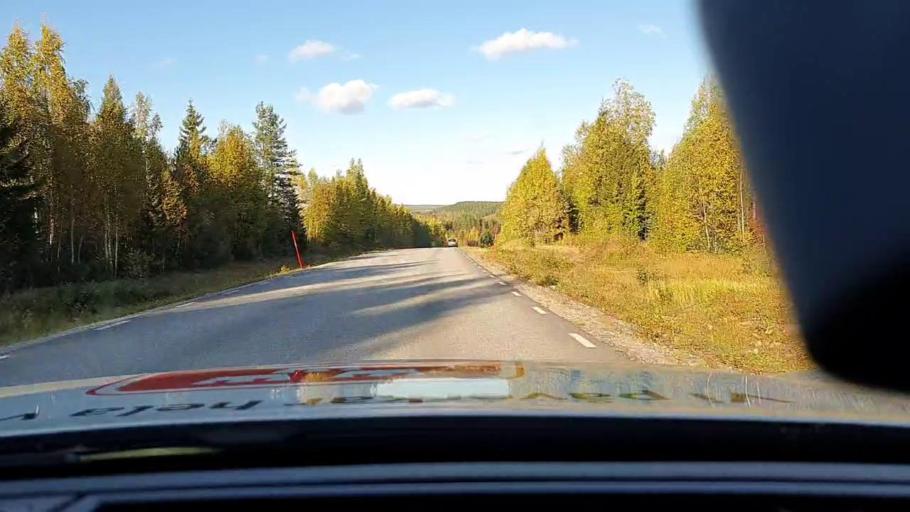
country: SE
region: Norrbotten
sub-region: Pitea Kommun
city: Norrfjarden
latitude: 65.5041
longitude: 21.4788
